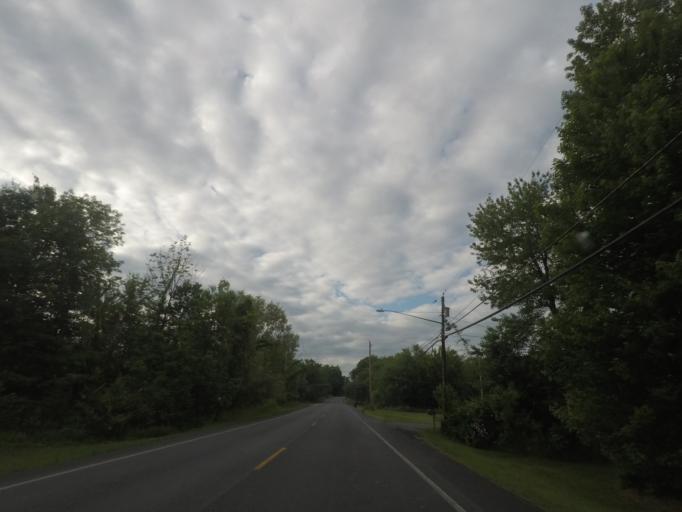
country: US
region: New York
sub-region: Ulster County
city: Plattekill
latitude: 41.5953
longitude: -74.1178
